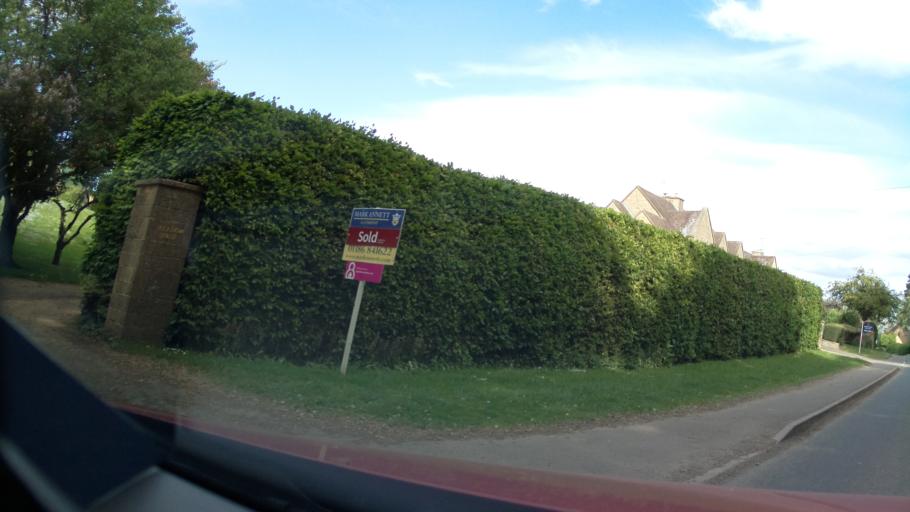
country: GB
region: England
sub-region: Gloucestershire
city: Chipping Campden
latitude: 52.0533
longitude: -1.7729
